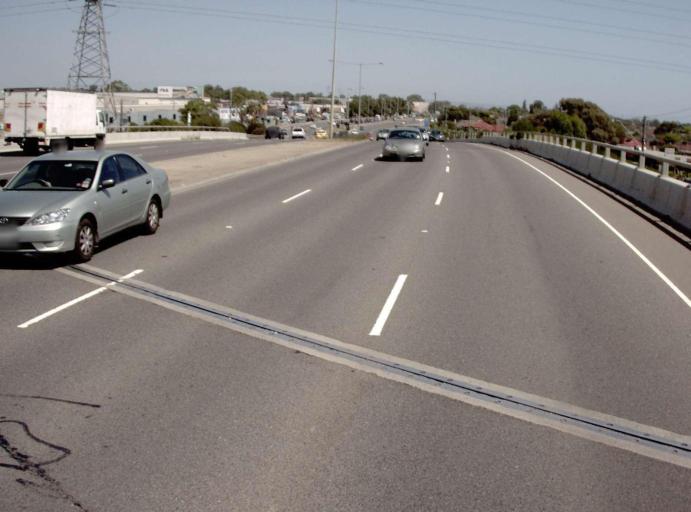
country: AU
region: Victoria
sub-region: Greater Dandenong
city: Springvale
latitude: -37.9391
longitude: 145.1401
